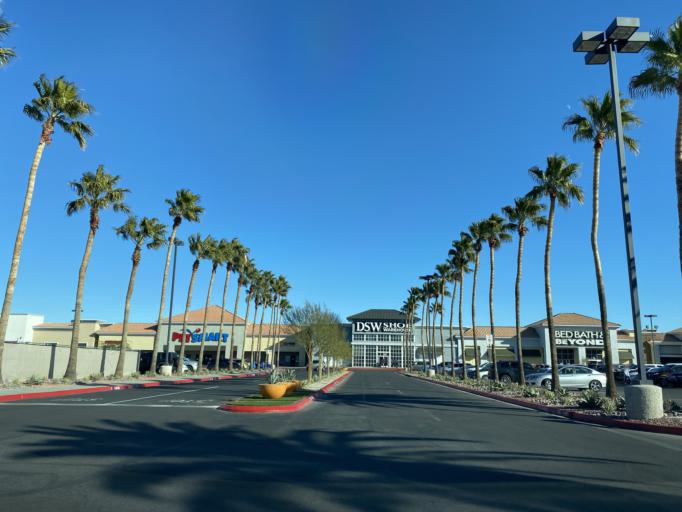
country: US
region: Nevada
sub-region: Clark County
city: Spring Valley
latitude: 36.1977
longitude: -115.2400
